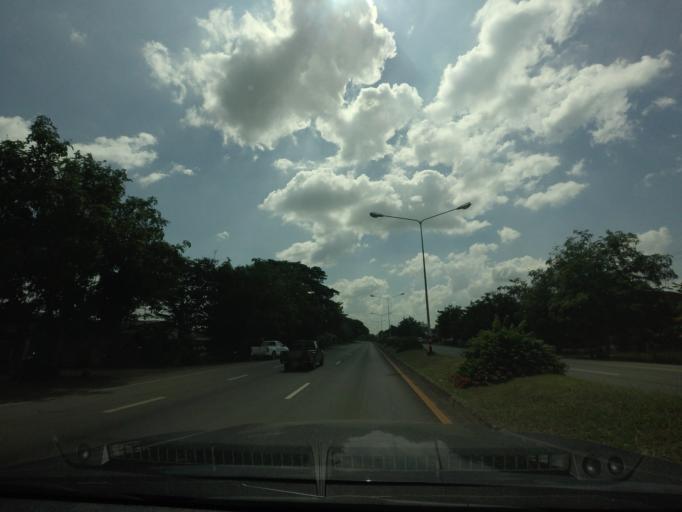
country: TH
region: Phetchabun
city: Nong Phai
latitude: 16.1310
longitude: 101.0446
